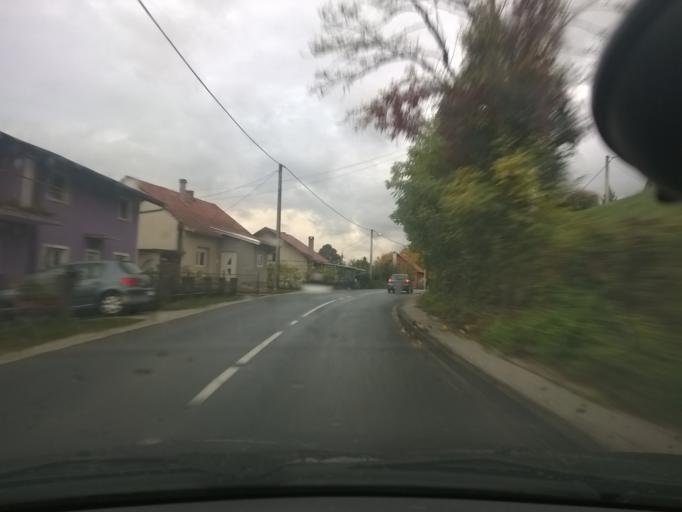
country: HR
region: Krapinsko-Zagorska
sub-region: Grad Krapina
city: Krapina
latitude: 46.1088
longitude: 15.8945
